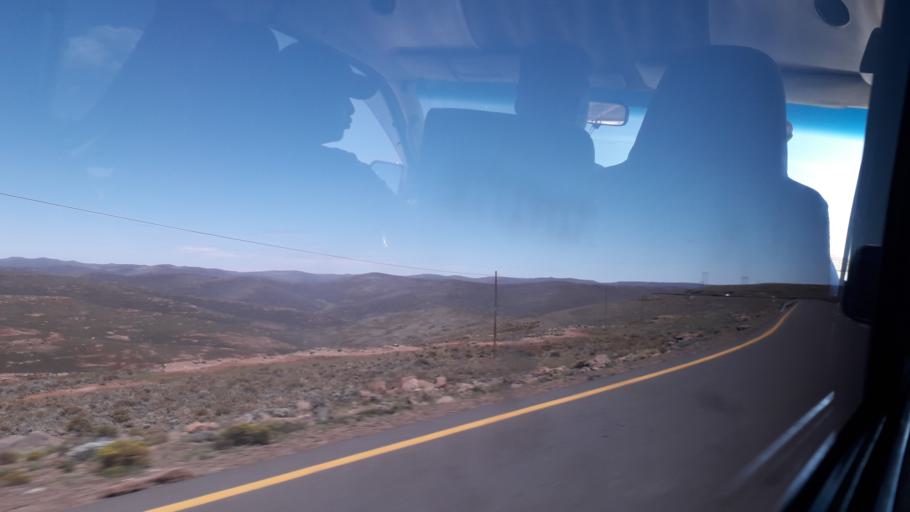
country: LS
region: Mokhotlong
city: Mokhotlong
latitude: -29.0227
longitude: 28.8565
